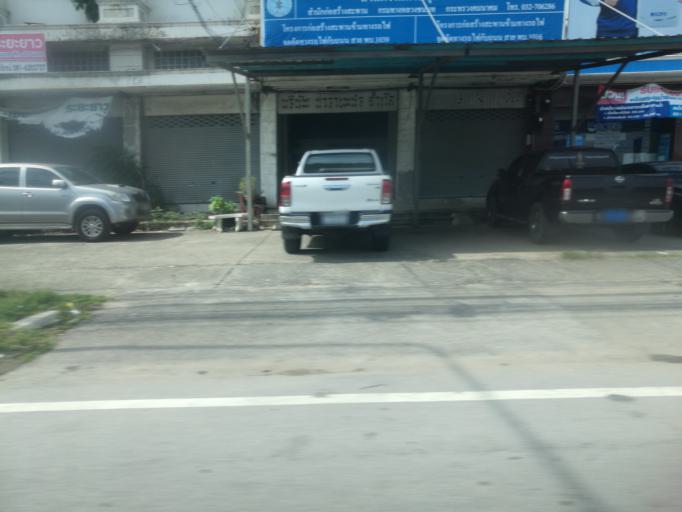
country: TH
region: Phetchaburi
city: Phetchaburi
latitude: 13.1084
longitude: 99.9329
